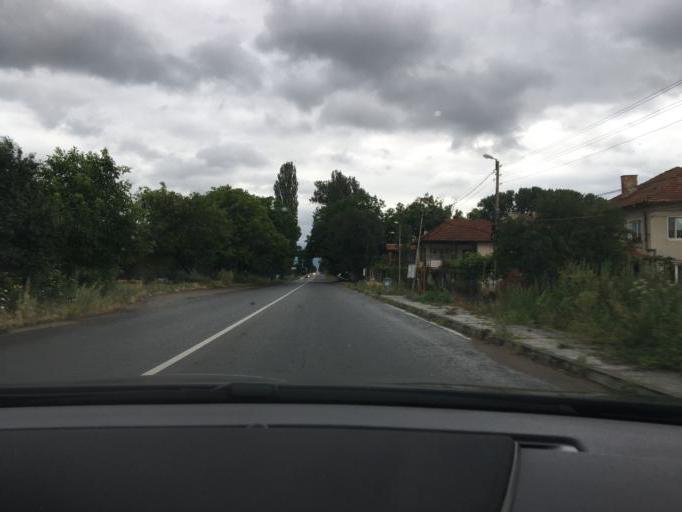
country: BG
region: Kyustendil
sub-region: Obshtina Kyustendil
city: Kyustendil
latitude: 42.2802
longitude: 22.7292
